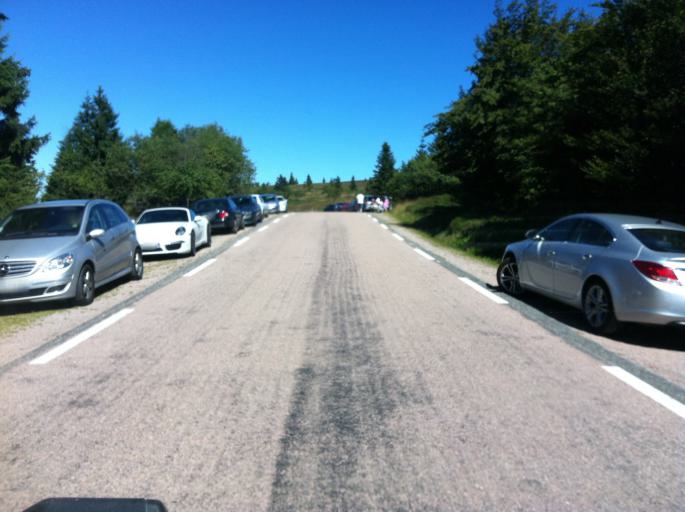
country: FR
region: Alsace
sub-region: Departement du Haut-Rhin
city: Soultzeren
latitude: 48.0933
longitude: 7.0606
